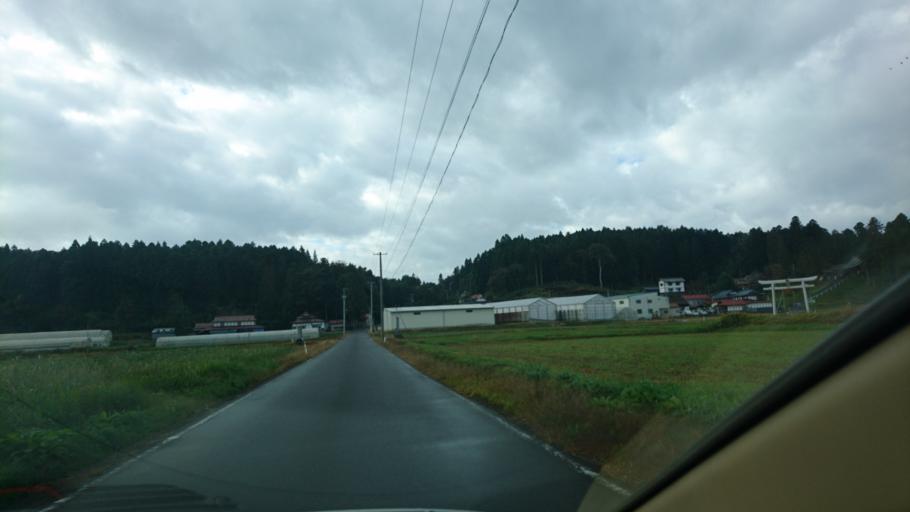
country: JP
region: Iwate
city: Ichinoseki
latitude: 38.7967
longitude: 140.9881
